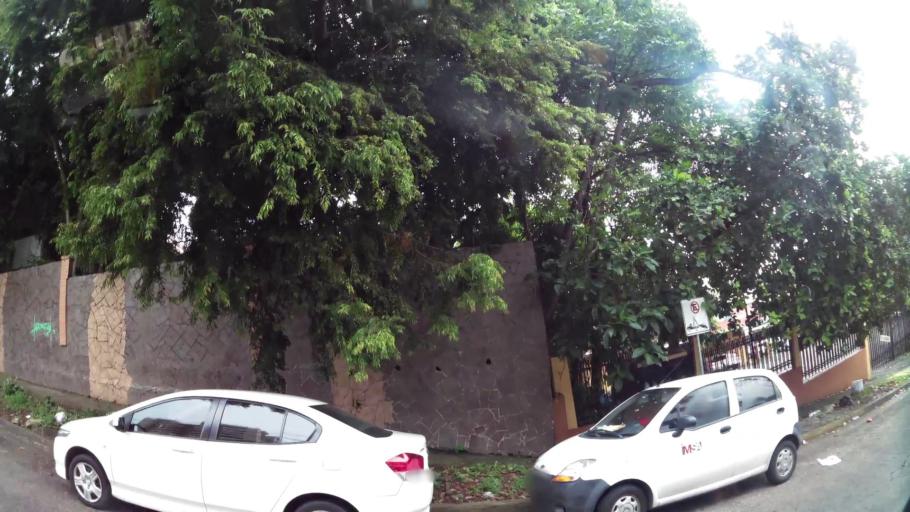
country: PA
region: Panama
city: Panama
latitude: 9.0120
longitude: -79.5333
